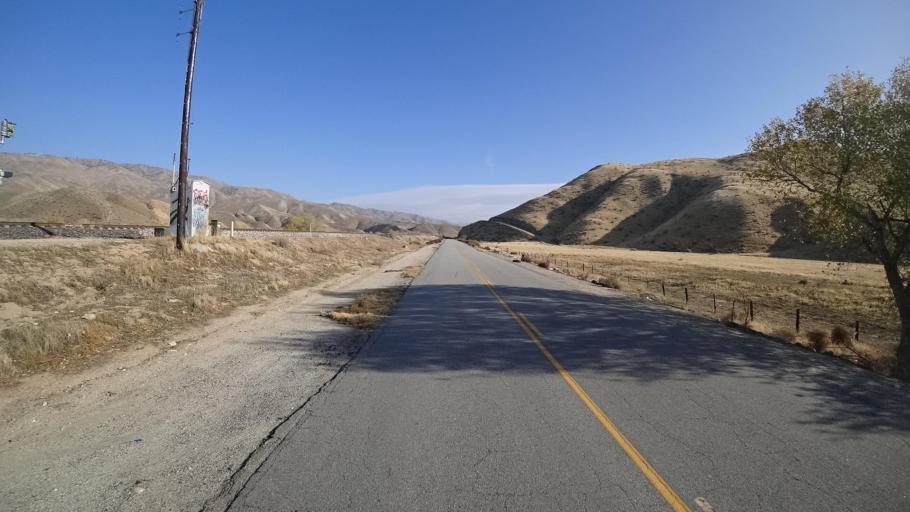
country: US
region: California
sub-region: Kern County
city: Arvin
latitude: 35.3221
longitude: -118.7115
